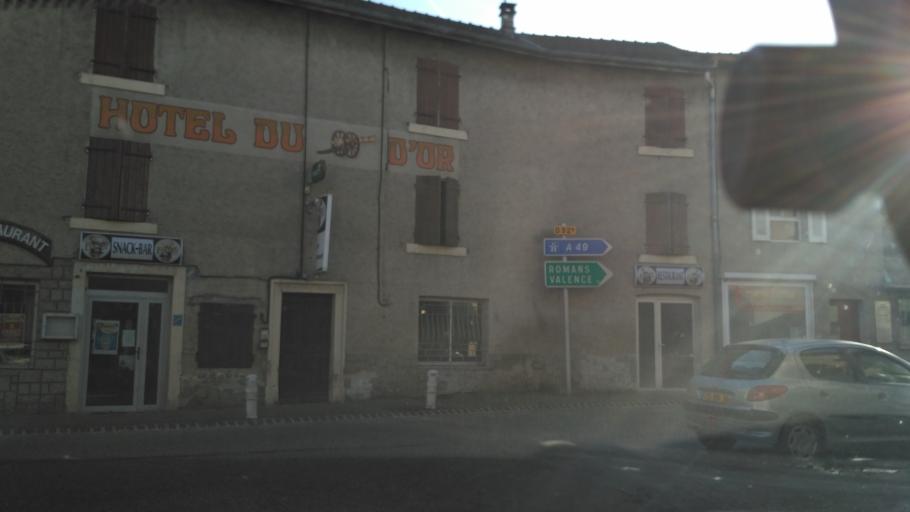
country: FR
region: Rhone-Alpes
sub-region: Departement de la Drome
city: Saint-Paul-les-Romans
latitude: 45.0703
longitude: 5.1332
